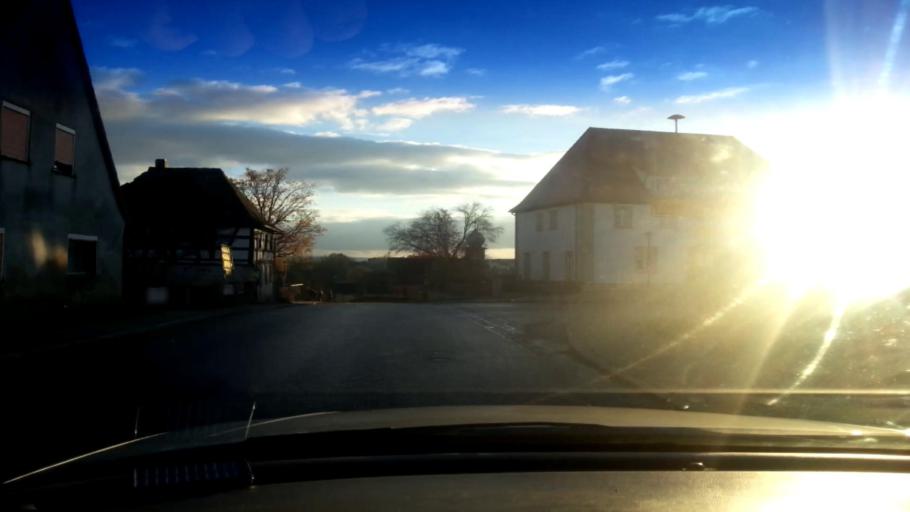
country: DE
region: Bavaria
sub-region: Upper Franconia
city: Buttenheim
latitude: 49.8266
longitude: 11.0279
